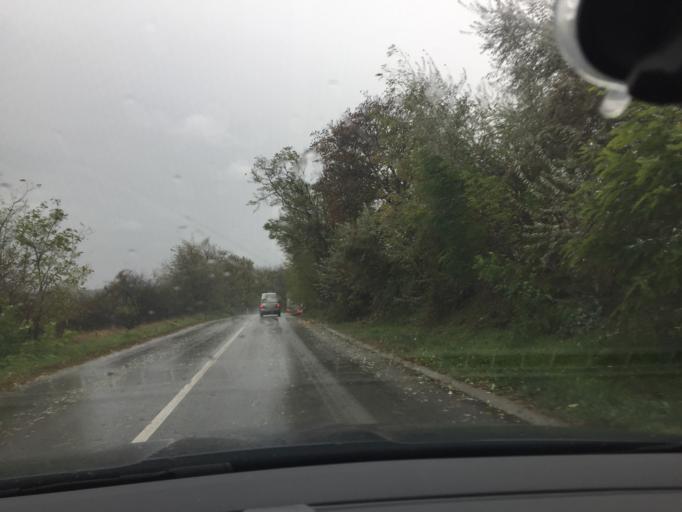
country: HU
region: Komarom-Esztergom
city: Tokod
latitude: 47.7037
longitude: 18.6312
